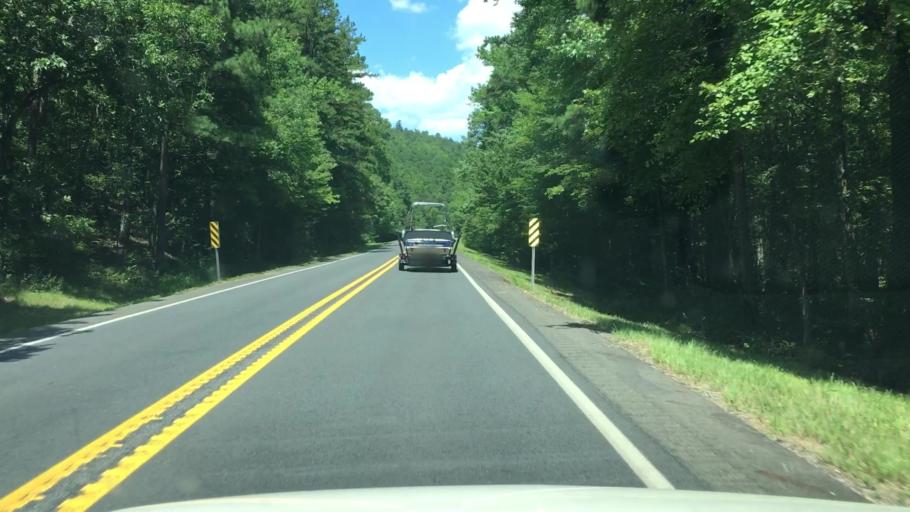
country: US
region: Arkansas
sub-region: Garland County
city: Lake Hamilton
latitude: 34.3574
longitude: -93.1788
